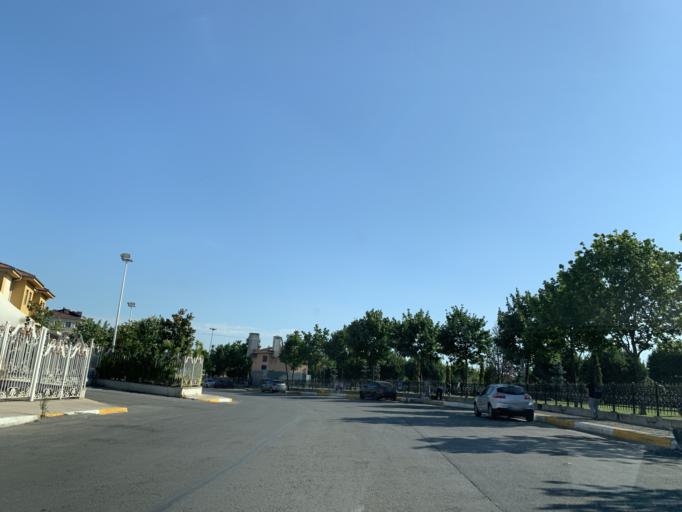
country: TR
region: Istanbul
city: Pendik
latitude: 40.8846
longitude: 29.2655
